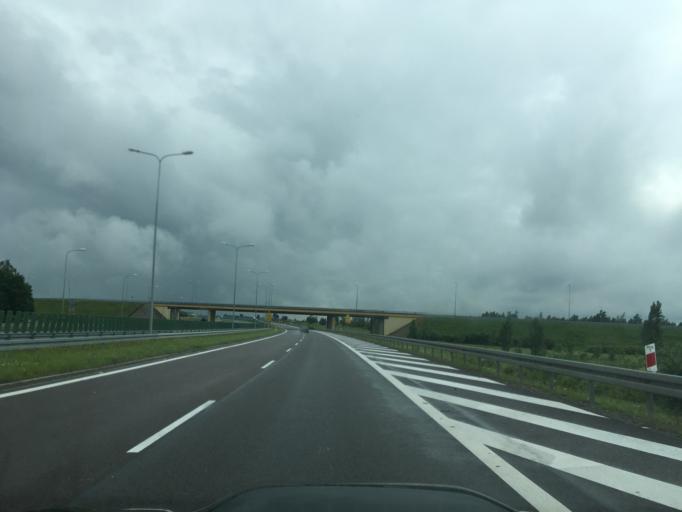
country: PL
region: Lublin Voivodeship
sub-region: Powiat pulawski
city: Zyrzyn
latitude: 51.4367
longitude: 22.1208
